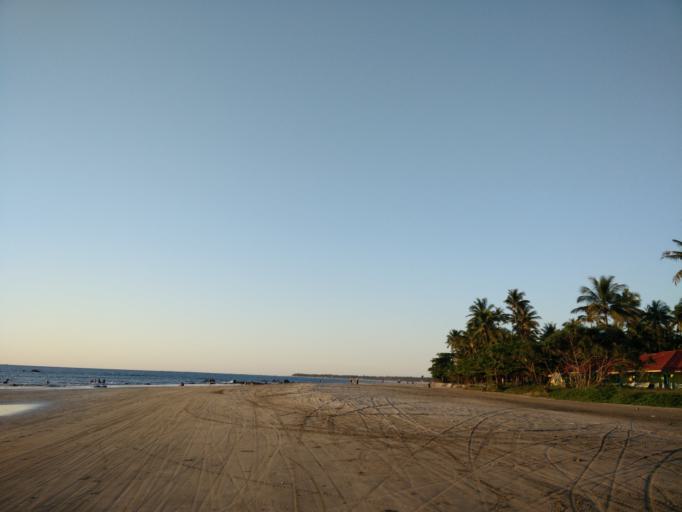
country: MM
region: Ayeyarwady
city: Pathein
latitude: 16.8368
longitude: 94.3920
